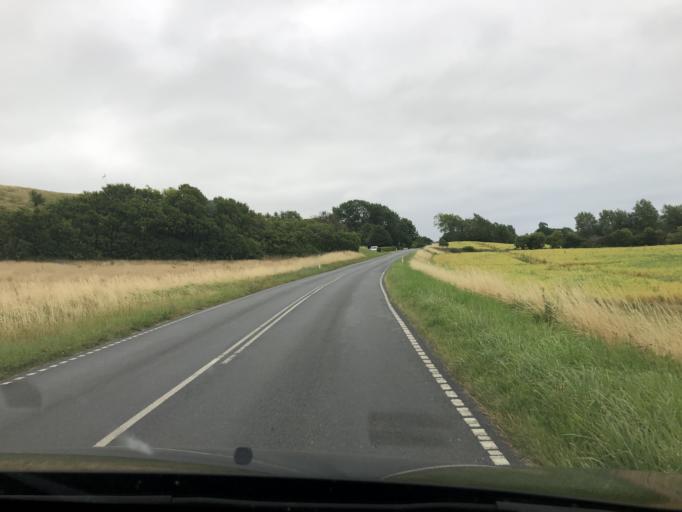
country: DK
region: South Denmark
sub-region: AEro Kommune
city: AEroskobing
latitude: 54.9211
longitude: 10.2794
